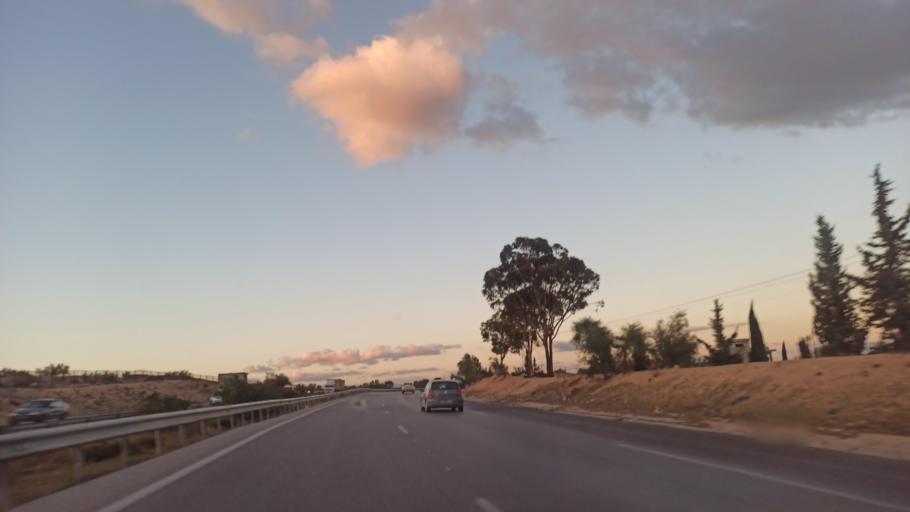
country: TN
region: Susah
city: Harqalah
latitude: 36.2298
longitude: 10.4133
